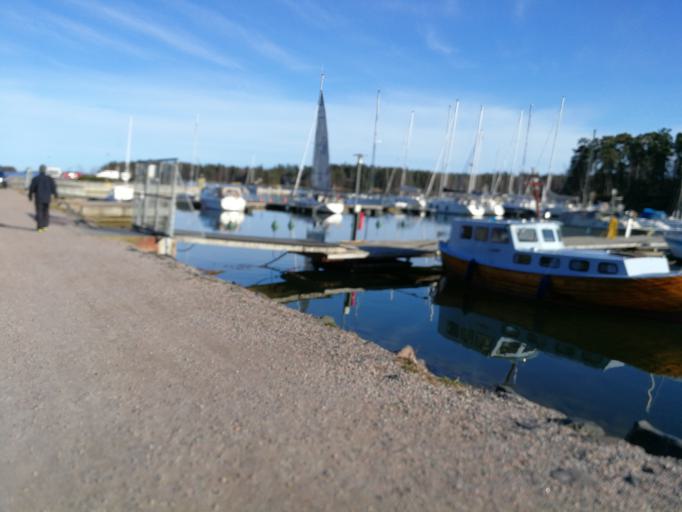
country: FI
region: Uusimaa
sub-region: Helsinki
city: Vantaa
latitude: 60.1997
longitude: 25.1390
